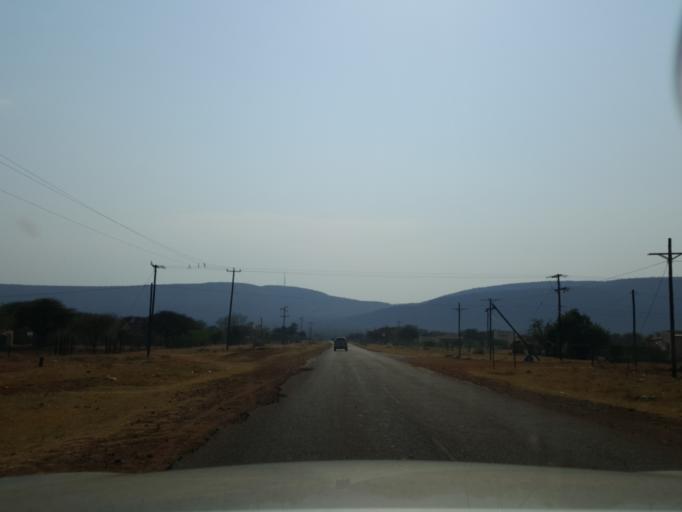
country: BW
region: South East
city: Lobatse
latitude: -25.2972
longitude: 25.8405
